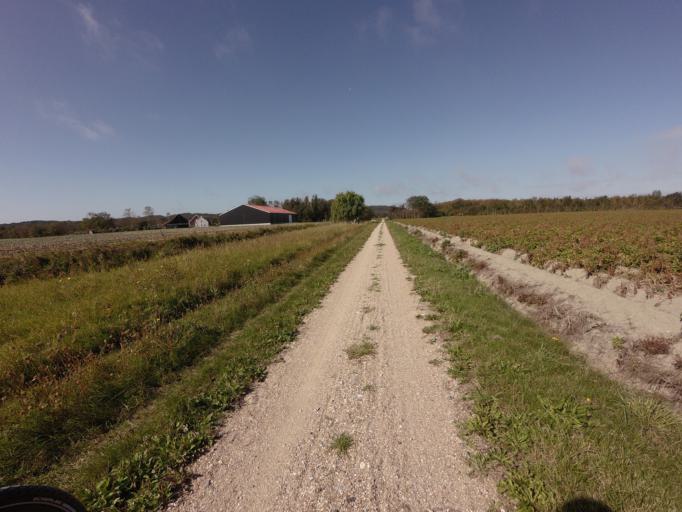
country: NL
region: Zeeland
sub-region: Gemeente Vlissingen
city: Vlissingen
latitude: 51.4911
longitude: 3.5194
